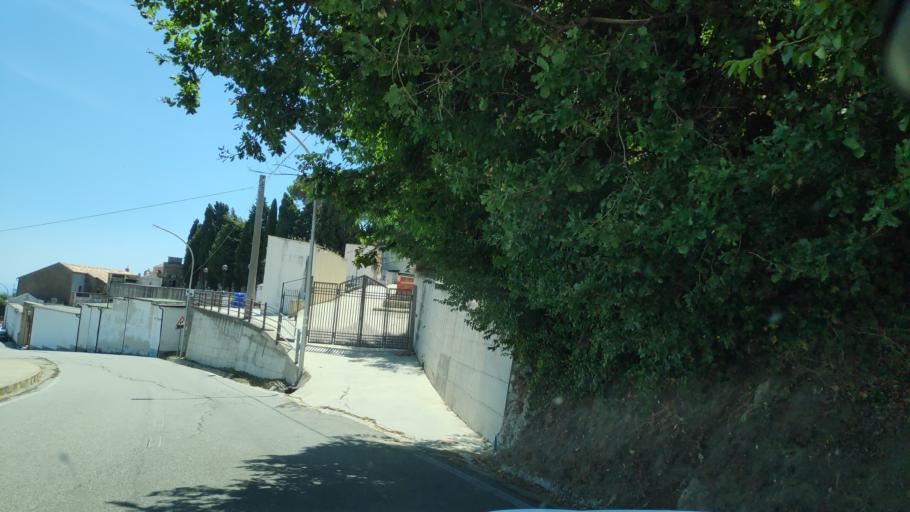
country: IT
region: Calabria
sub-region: Provincia di Catanzaro
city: Gasperina
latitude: 38.7370
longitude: 16.5126
